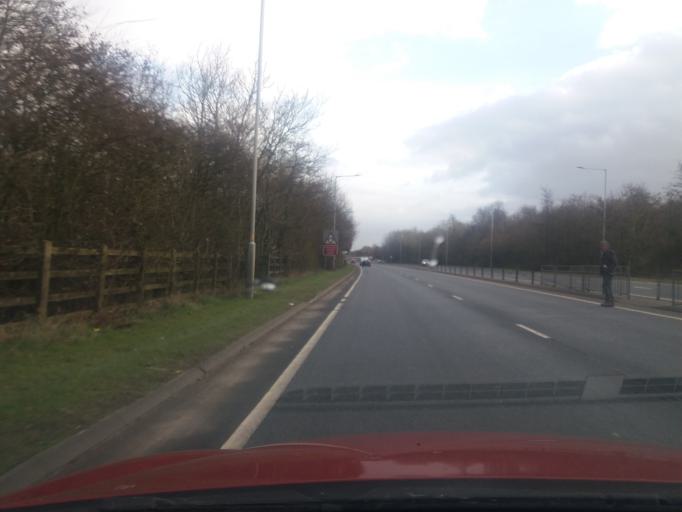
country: GB
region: England
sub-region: Lancashire
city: Clayton-le-Woods
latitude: 53.7320
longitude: -2.6759
